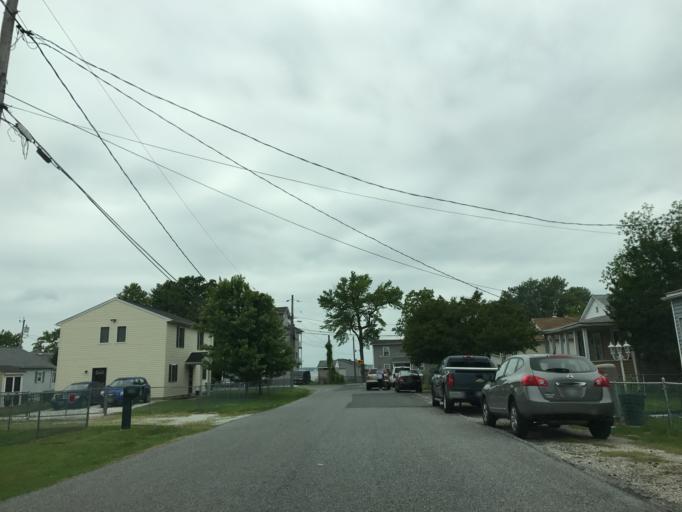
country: US
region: Maryland
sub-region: Baltimore County
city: Dundalk
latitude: 39.2422
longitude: -76.5155
